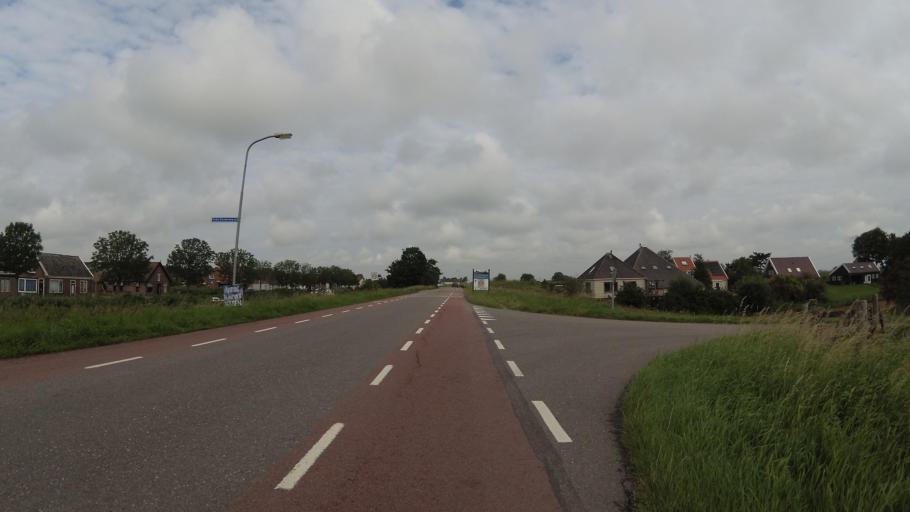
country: NL
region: North Holland
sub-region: Gemeente Schagen
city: Schagen
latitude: 52.8314
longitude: 4.8134
